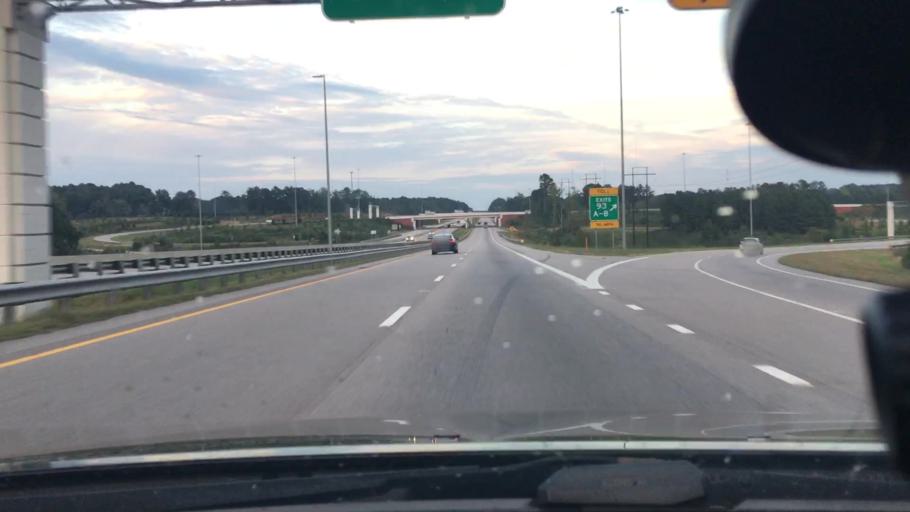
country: US
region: North Carolina
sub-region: Wake County
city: Apex
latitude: 35.6945
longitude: -78.8768
